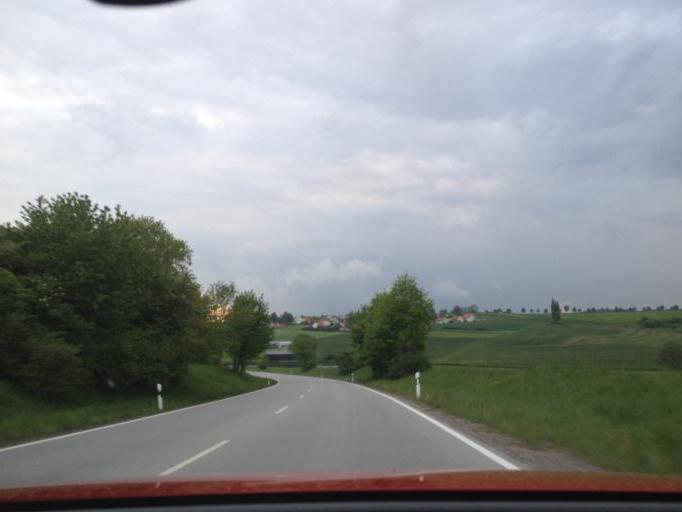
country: DE
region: Bavaria
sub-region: Upper Palatinate
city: Gebenbach
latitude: 49.5390
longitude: 11.8869
